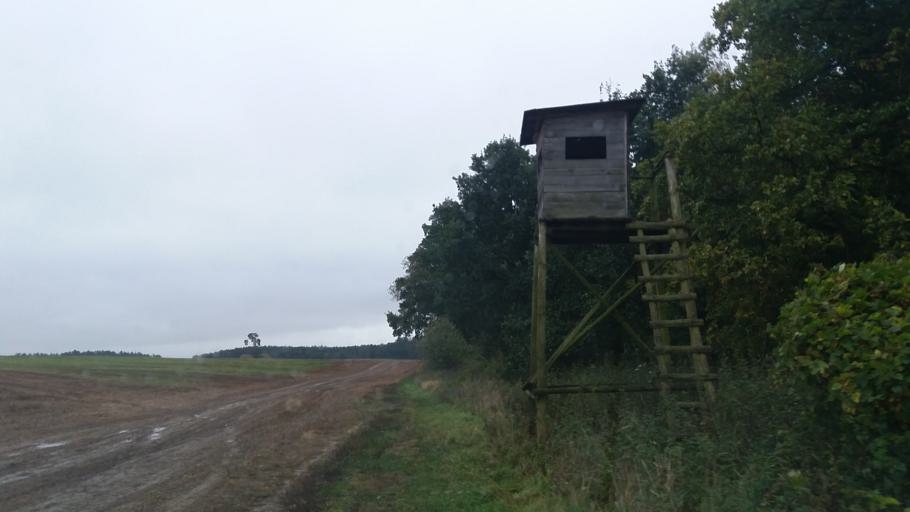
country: PL
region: West Pomeranian Voivodeship
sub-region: Powiat choszczenski
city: Pelczyce
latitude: 53.0741
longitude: 15.2956
